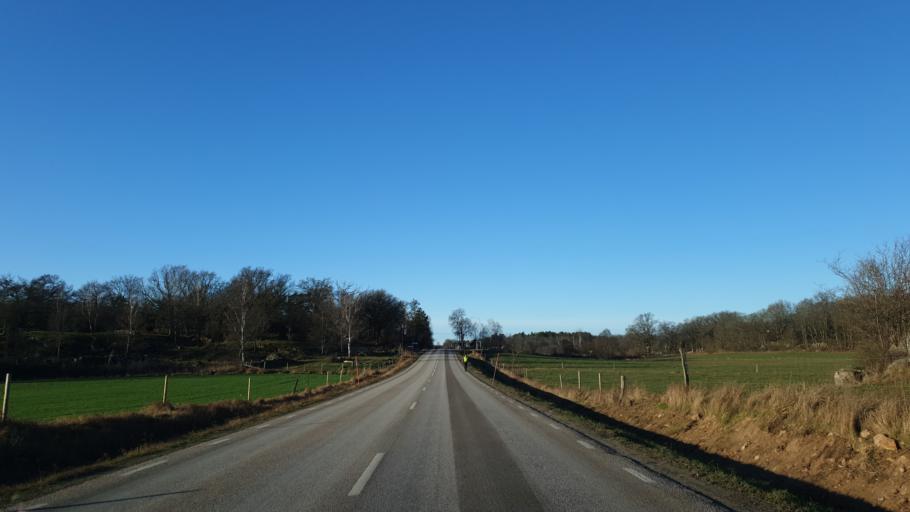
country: SE
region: Blekinge
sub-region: Ronneby Kommun
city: Ronneby
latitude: 56.1931
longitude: 15.3493
